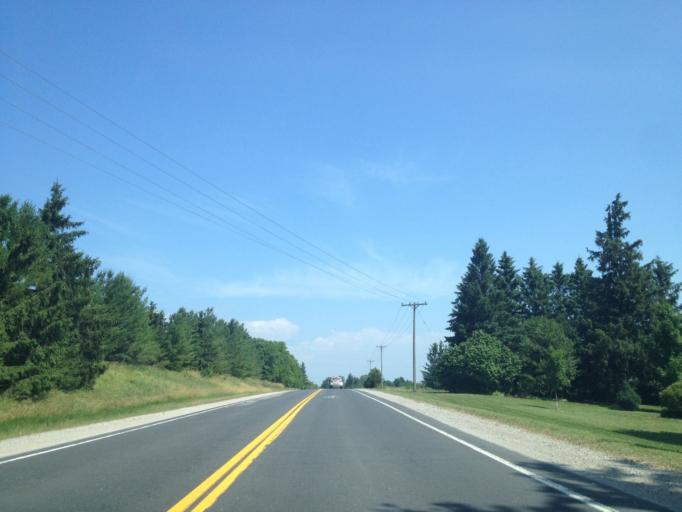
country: CA
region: Ontario
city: Huron East
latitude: 43.3772
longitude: -81.2193
